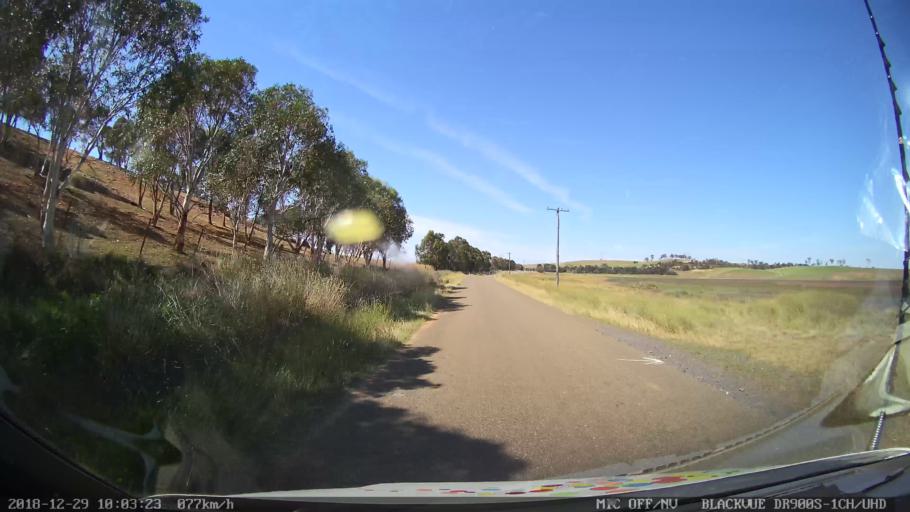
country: AU
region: New South Wales
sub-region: Goulburn Mulwaree
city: Goulburn
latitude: -34.8104
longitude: 149.4601
